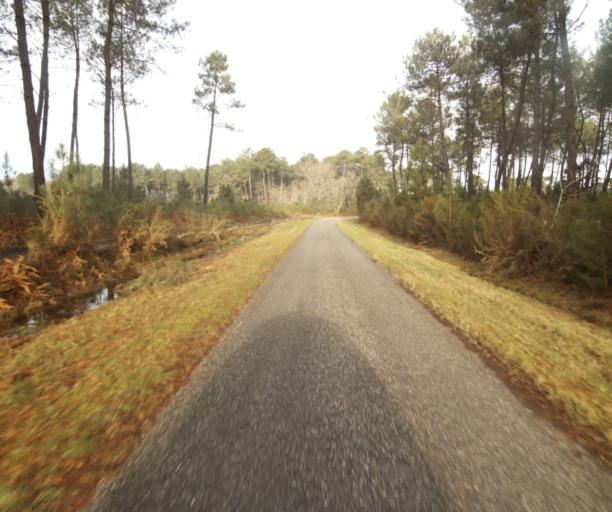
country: FR
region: Aquitaine
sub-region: Departement des Landes
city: Gabarret
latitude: 44.0695
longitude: 0.0900
